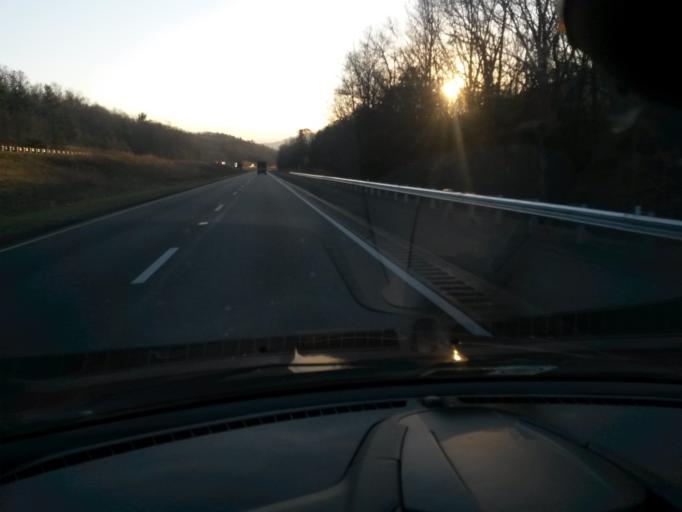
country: US
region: Virginia
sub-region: Alleghany County
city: Clifton Forge
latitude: 37.8453
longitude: -79.6367
